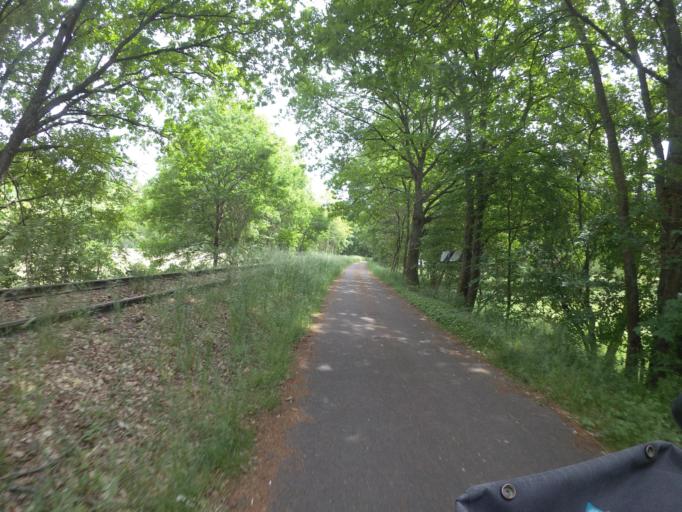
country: DE
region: Rheinland-Pfalz
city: Rathsweiler
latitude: 49.5998
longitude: 7.4788
